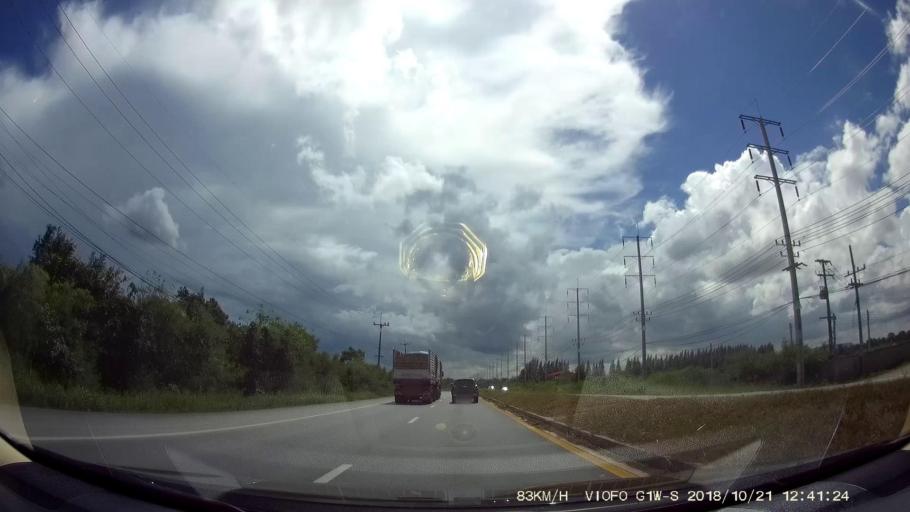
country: TH
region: Nakhon Ratchasima
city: Amphoe Sikhiu
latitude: 15.0130
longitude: 101.6871
